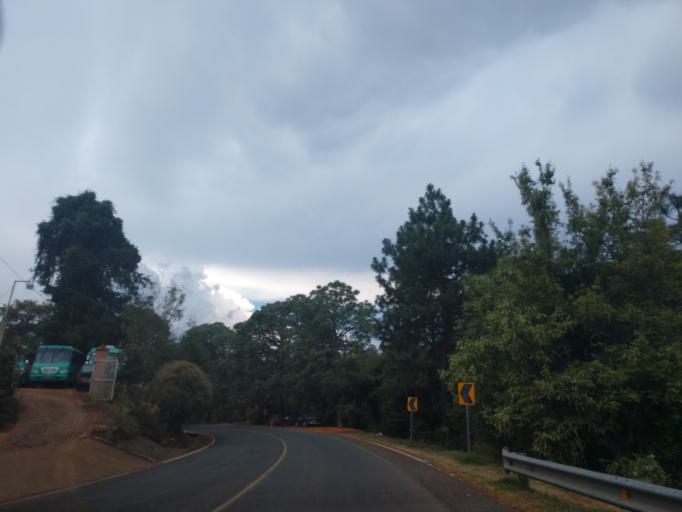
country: MX
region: Jalisco
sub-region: Mazamitla
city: Mazamitla
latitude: 19.9212
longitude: -103.0295
